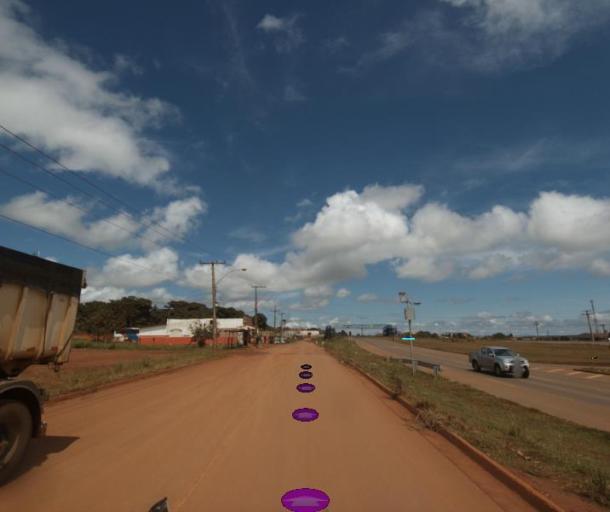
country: BR
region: Federal District
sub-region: Brasilia
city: Brasilia
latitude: -15.7519
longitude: -48.3251
